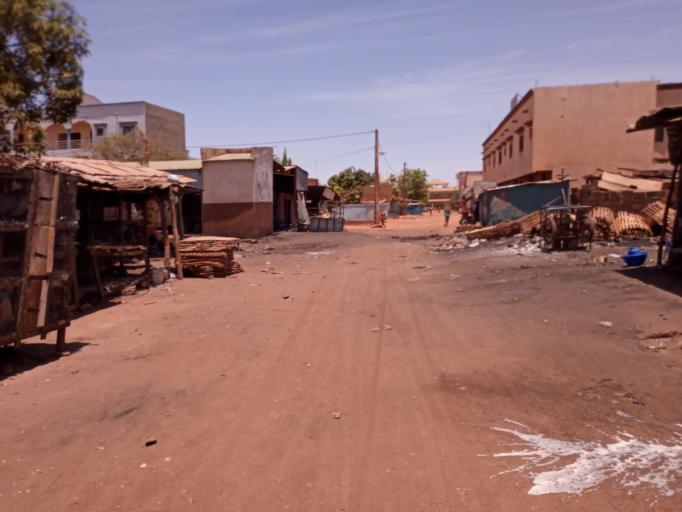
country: ML
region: Bamako
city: Bamako
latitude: 12.5841
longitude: -7.9560
